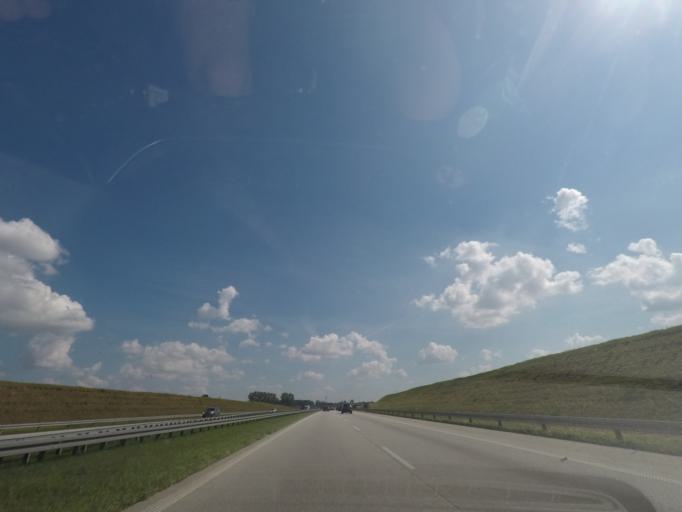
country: PL
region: Lodz Voivodeship
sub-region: Powiat zgierski
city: Strykow
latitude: 51.8725
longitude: 19.6519
